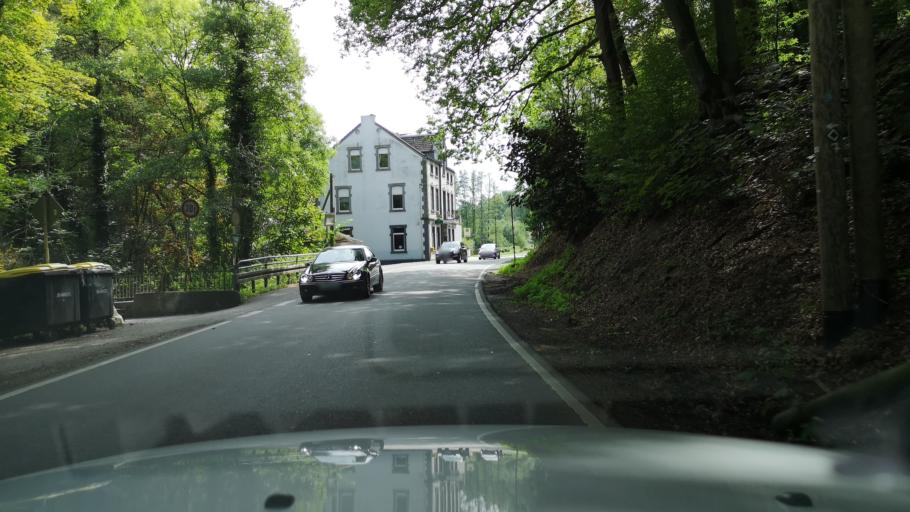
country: DE
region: North Rhine-Westphalia
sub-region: Regierungsbezirk Dusseldorf
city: Wuppertal
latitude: 51.3400
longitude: 7.1366
